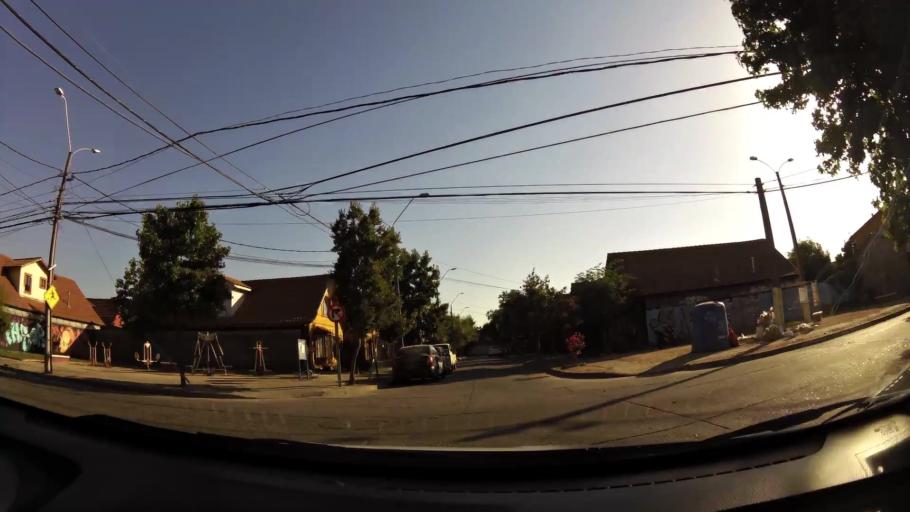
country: CL
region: Maule
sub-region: Provincia de Talca
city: Talca
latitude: -35.4411
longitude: -71.6879
